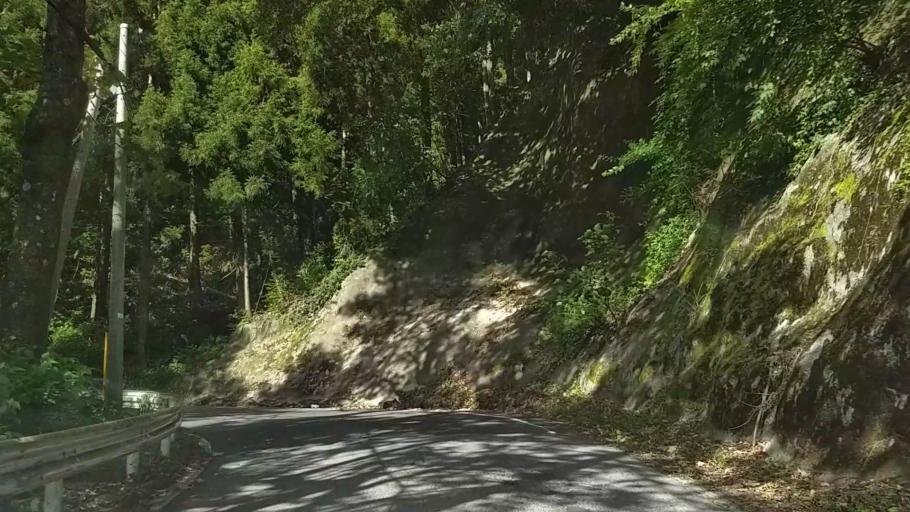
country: JP
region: Yamanashi
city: Uenohara
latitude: 35.5623
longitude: 139.1475
